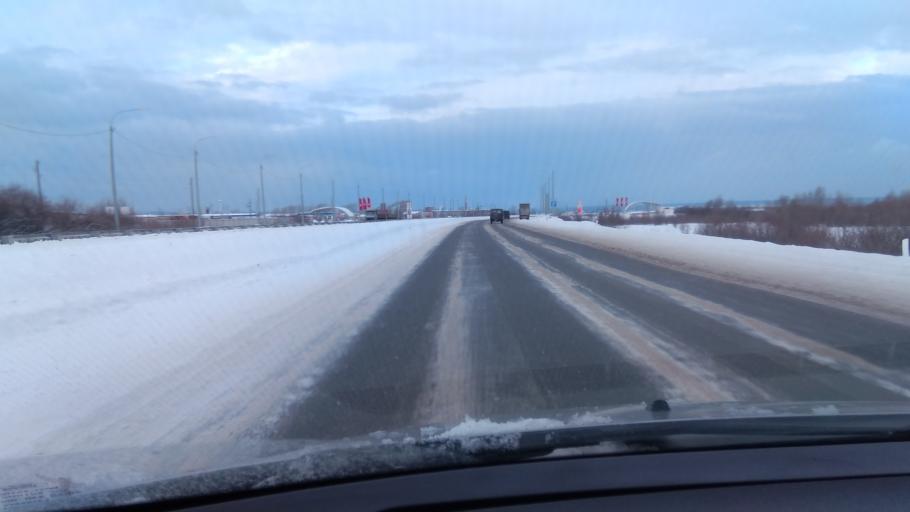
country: RU
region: Sverdlovsk
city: Tsementnyy
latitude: 57.4643
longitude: 60.1865
